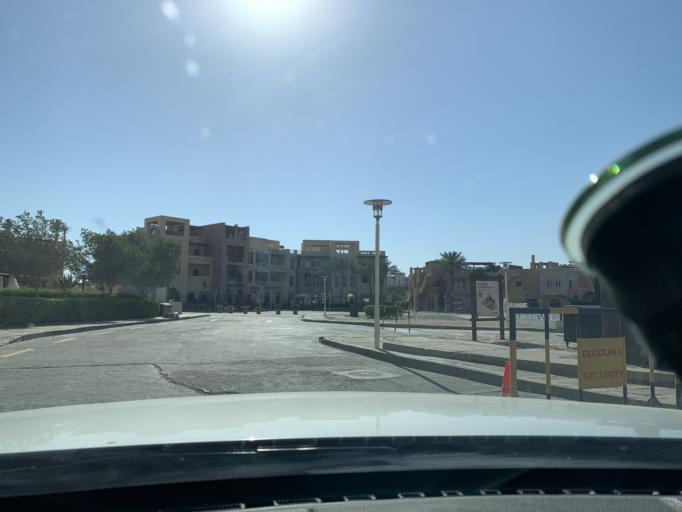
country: EG
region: Red Sea
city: El Gouna
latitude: 27.4069
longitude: 33.6749
